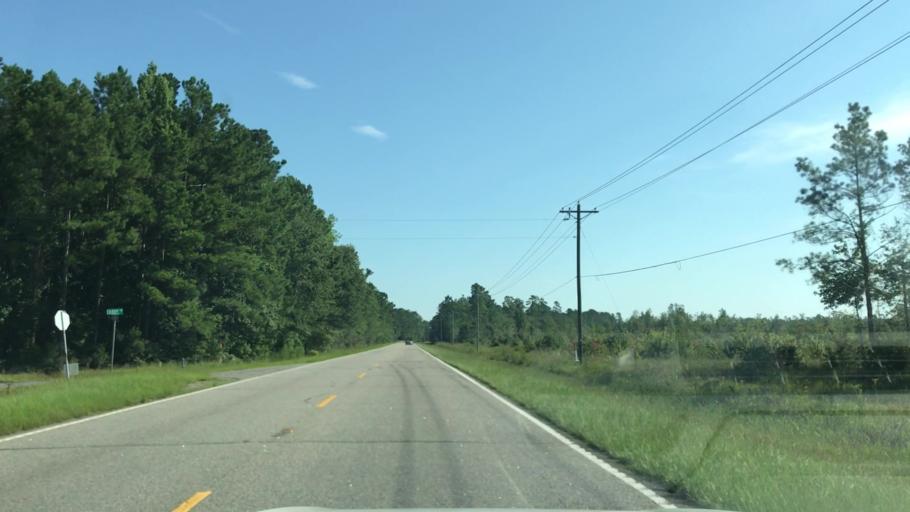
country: US
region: South Carolina
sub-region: Georgetown County
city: Georgetown
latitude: 33.5196
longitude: -79.2465
